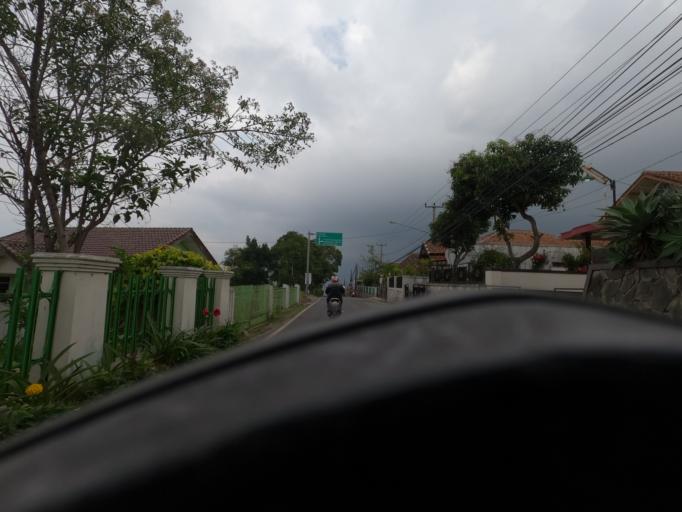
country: ID
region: West Java
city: Cimahi
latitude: -6.8167
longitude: 107.5461
